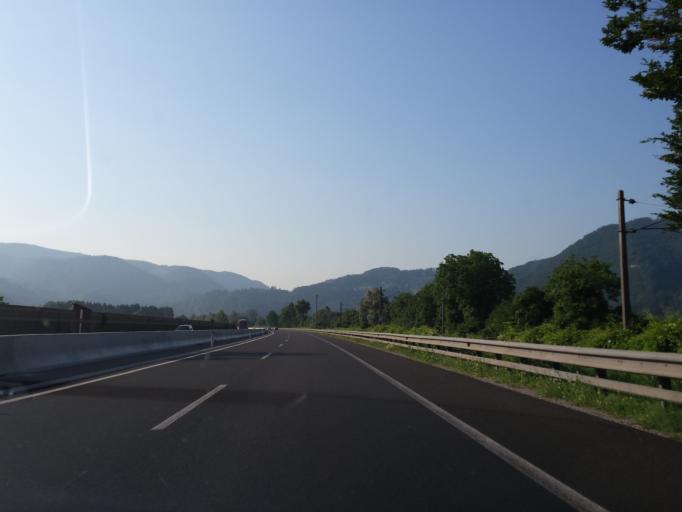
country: AT
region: Styria
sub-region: Politischer Bezirk Graz-Umgebung
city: Frohnleiten
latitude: 47.2427
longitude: 15.3191
